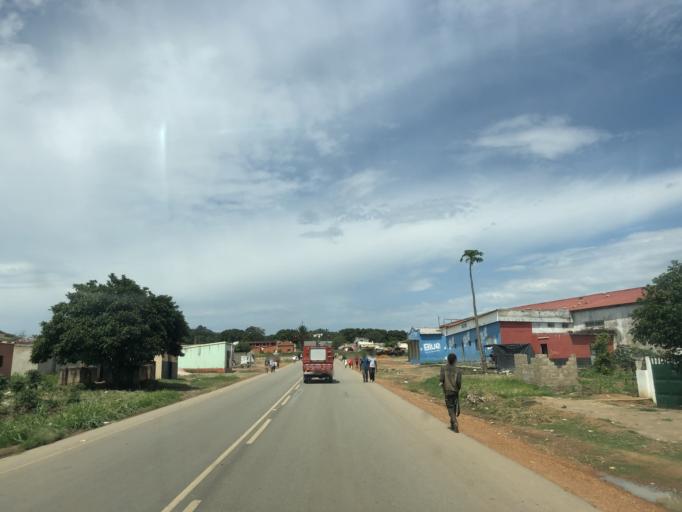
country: AO
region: Cuanza Sul
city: Quibala
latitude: -10.7357
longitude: 14.9842
